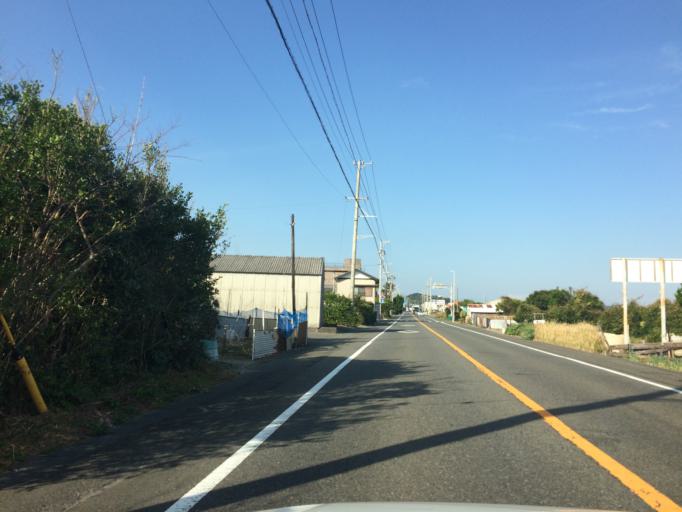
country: JP
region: Shizuoka
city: Sagara
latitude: 34.6587
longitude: 138.1938
